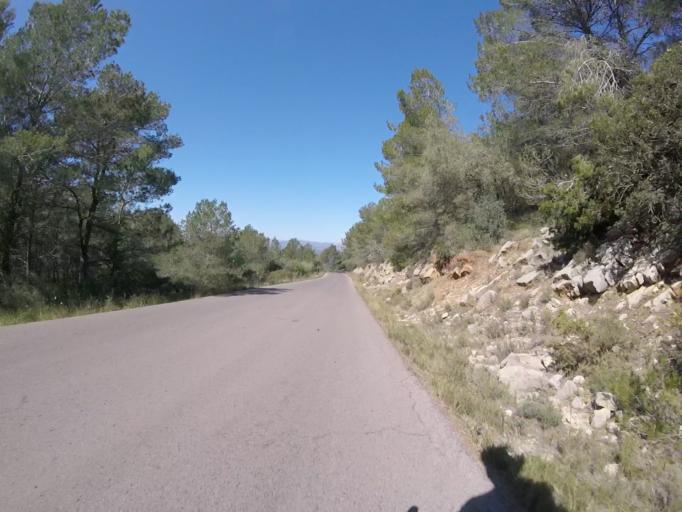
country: ES
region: Valencia
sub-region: Provincia de Castello
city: Cervera del Maestre
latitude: 40.4080
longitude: 0.1960
